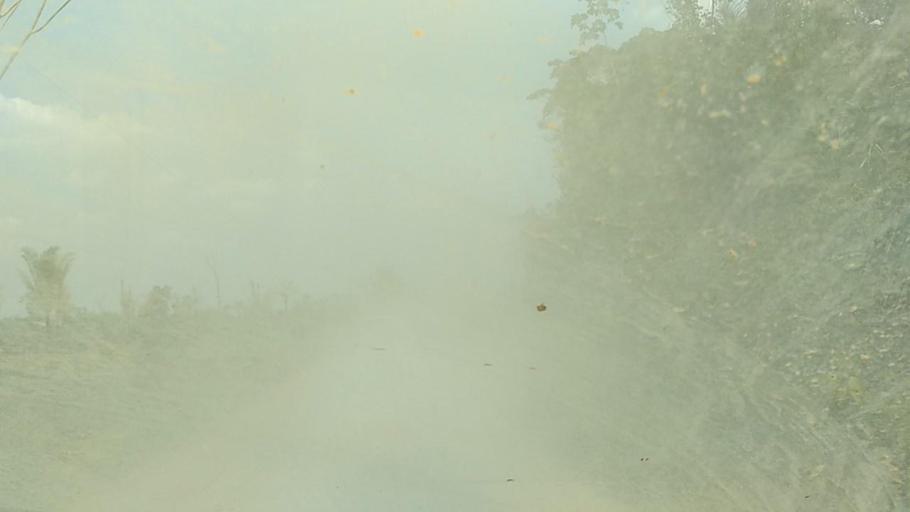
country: BR
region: Rondonia
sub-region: Porto Velho
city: Porto Velho
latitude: -8.7281
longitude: -63.3103
